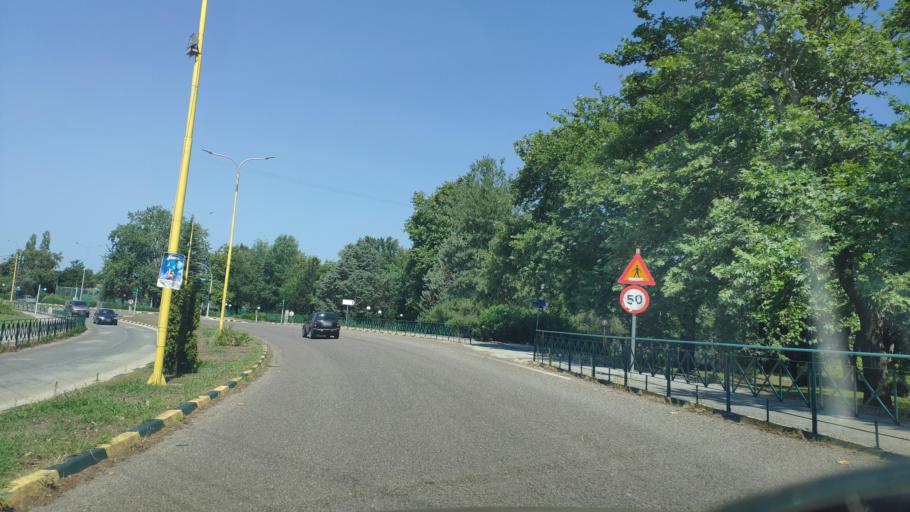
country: GR
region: Epirus
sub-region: Nomos Artas
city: Arta
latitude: 39.1670
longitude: 20.9881
